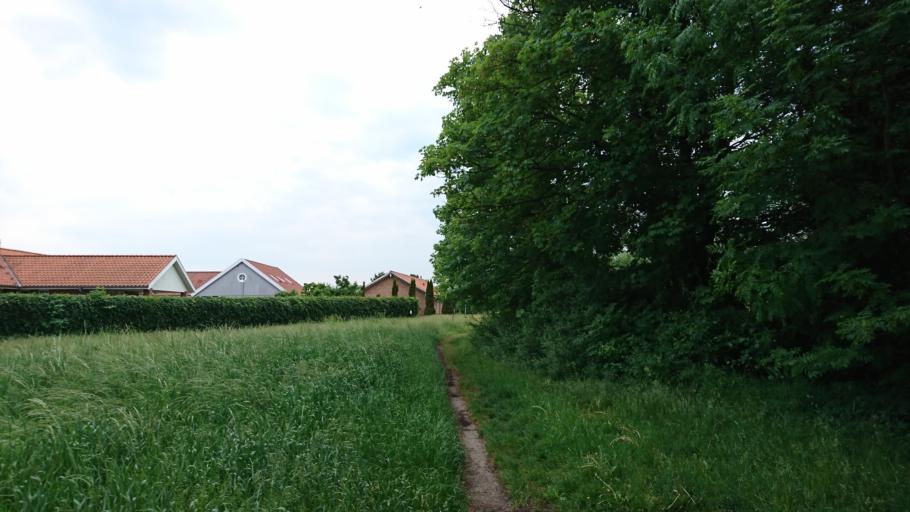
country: DK
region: Capital Region
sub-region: Ballerup Kommune
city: Malov
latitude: 55.7467
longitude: 12.3360
